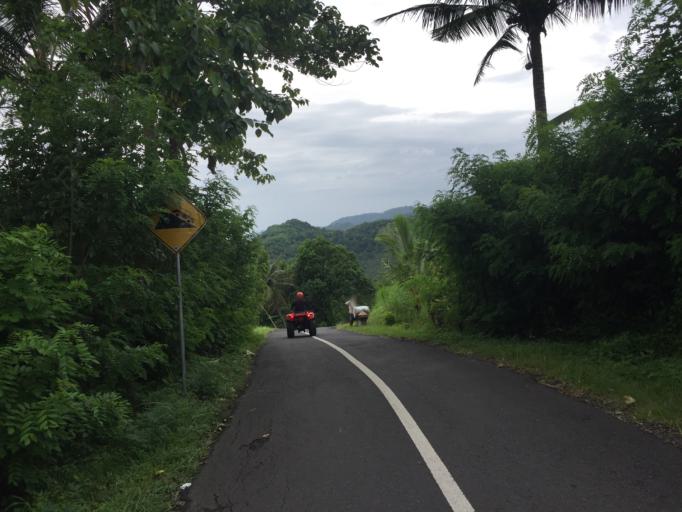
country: ID
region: Bali
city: Banjar Kawan
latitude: -8.4745
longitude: 115.5195
